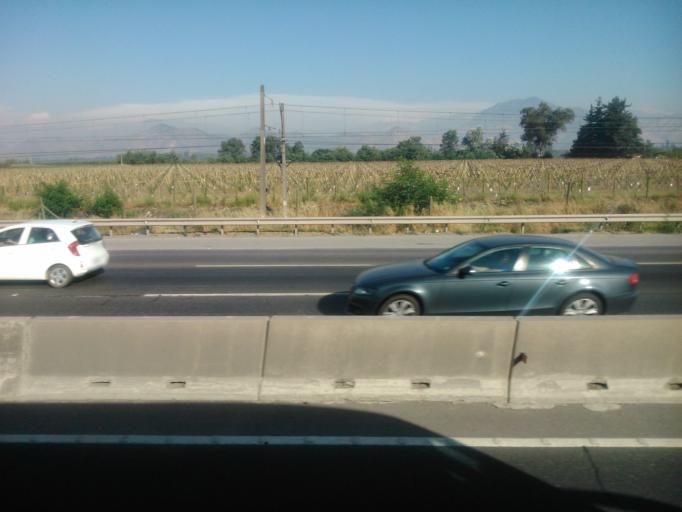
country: CL
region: Santiago Metropolitan
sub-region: Provincia de Maipo
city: Buin
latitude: -33.6723
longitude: -70.7225
